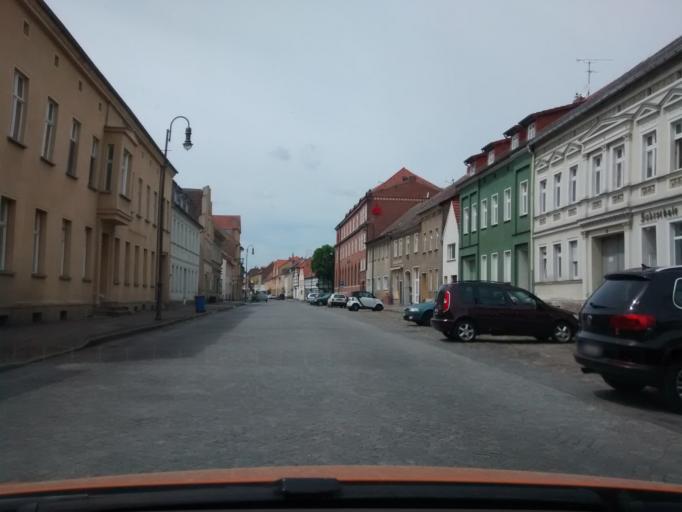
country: DE
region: Brandenburg
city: Juterbog
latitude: 51.9906
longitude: 13.0829
